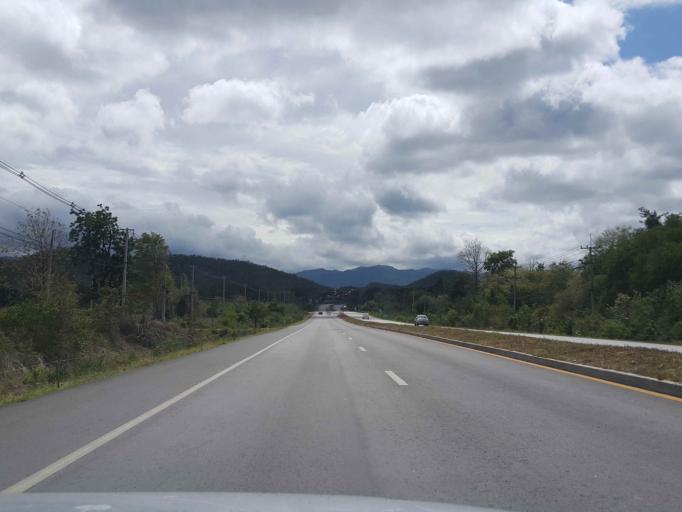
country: TH
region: Tak
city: Tak
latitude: 16.8251
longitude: 99.0848
